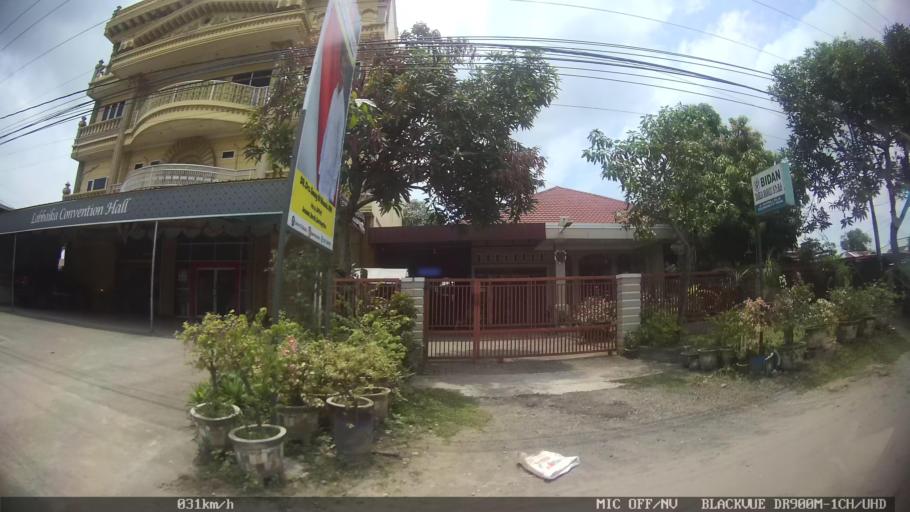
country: ID
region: North Sumatra
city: Labuhan Deli
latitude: 3.6801
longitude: 98.6705
